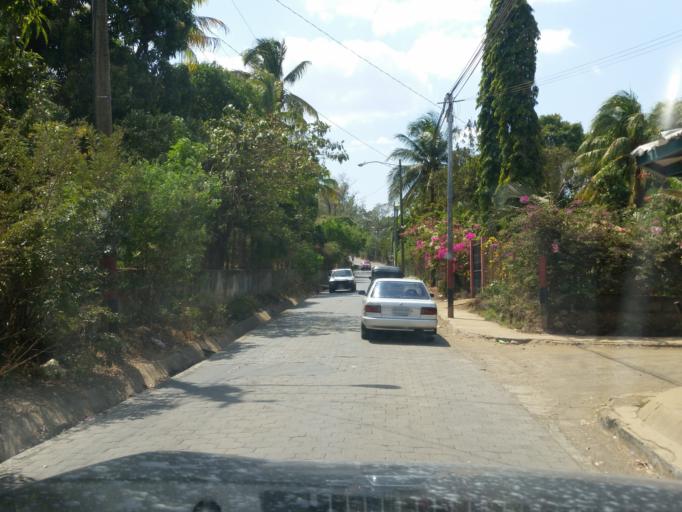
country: NI
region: Masaya
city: Ticuantepe
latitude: 12.0692
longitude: -86.2036
